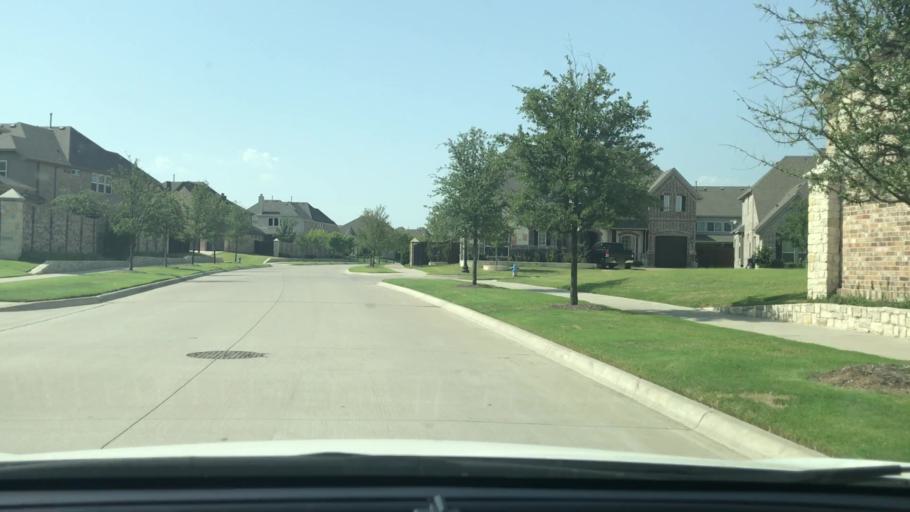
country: US
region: Texas
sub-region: Collin County
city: Frisco
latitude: 33.1320
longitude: -96.7646
